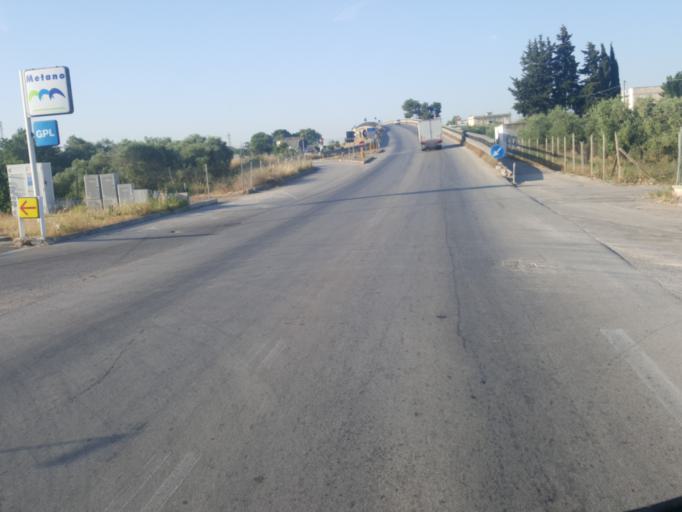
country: IT
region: Apulia
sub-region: Provincia di Foggia
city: Cerignola
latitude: 41.3193
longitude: 15.9001
